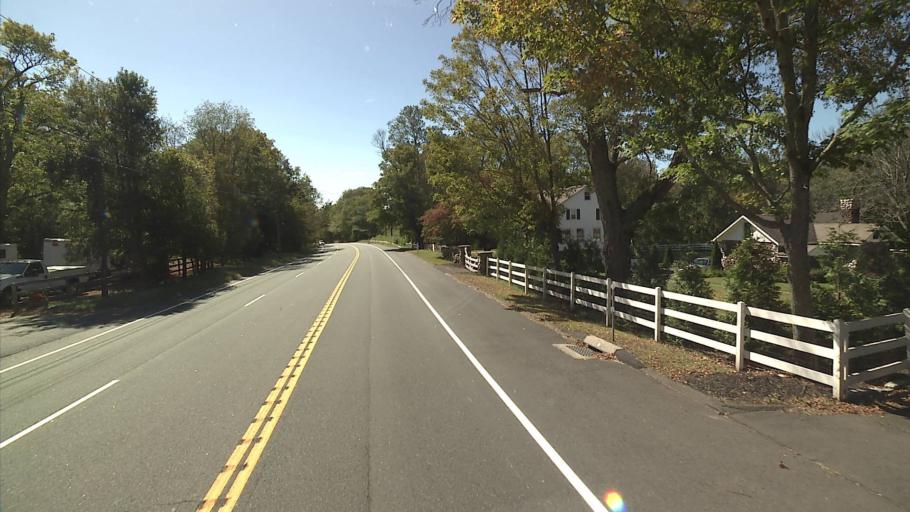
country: US
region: Connecticut
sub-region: New Haven County
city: Woodbridge
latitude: 41.3987
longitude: -72.9743
